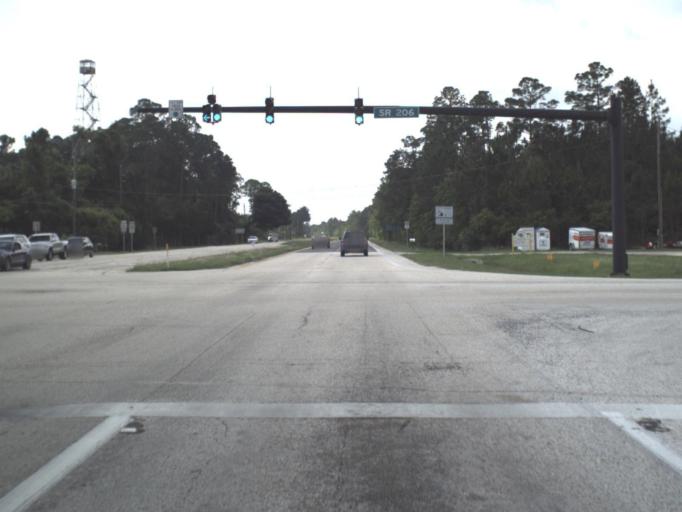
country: US
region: Florida
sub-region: Saint Johns County
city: Saint Augustine Shores
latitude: 29.7567
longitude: -81.3130
